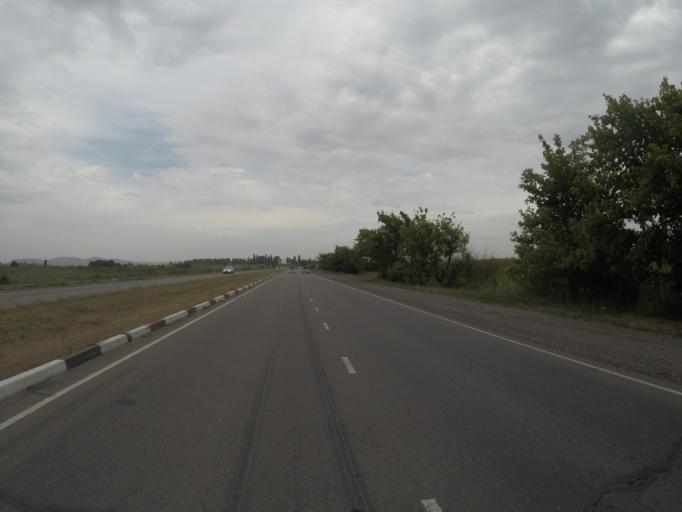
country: KG
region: Chuy
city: Kant
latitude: 42.9363
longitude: 74.7706
